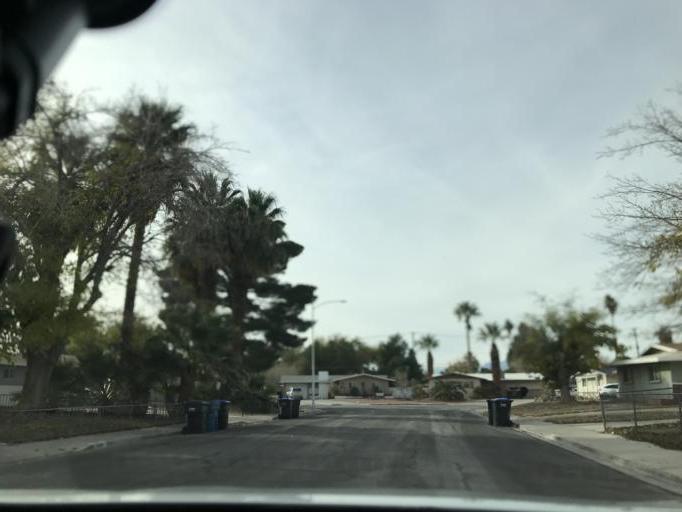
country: US
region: Nevada
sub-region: Clark County
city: Las Vegas
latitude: 36.1716
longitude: -115.1686
